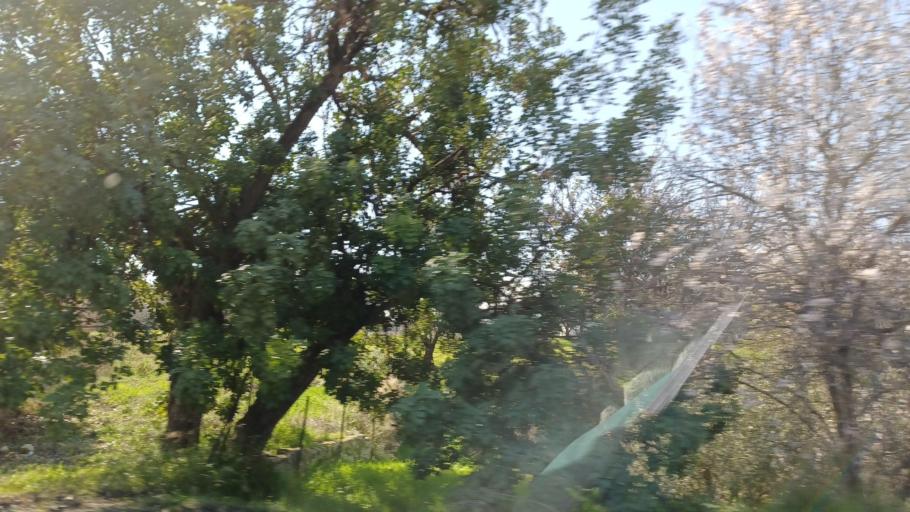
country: CY
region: Limassol
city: Pelendri
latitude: 34.8071
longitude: 32.9145
